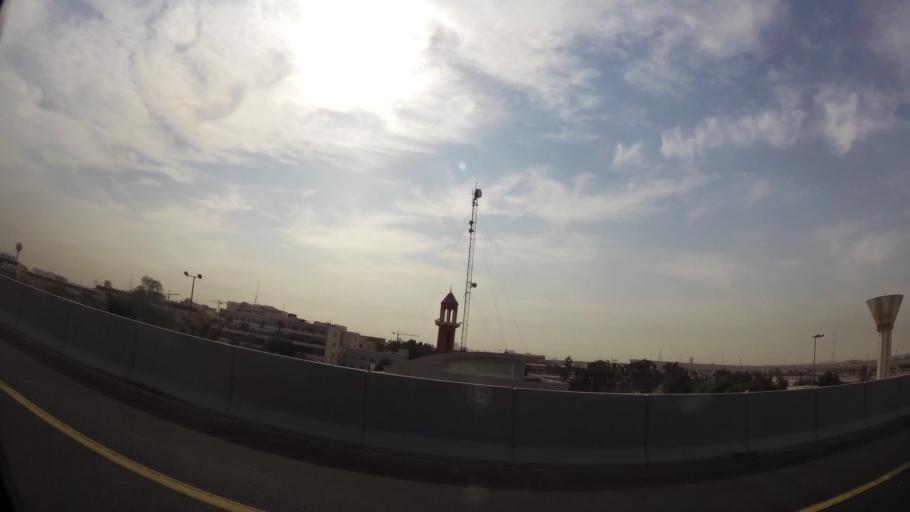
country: KW
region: Al Asimah
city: Ar Rabiyah
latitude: 29.3276
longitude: 47.8994
